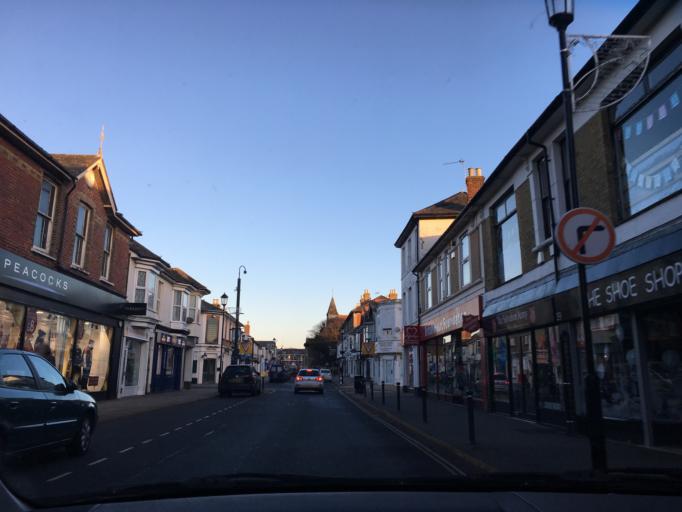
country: GB
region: England
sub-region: Isle of Wight
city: Shanklin
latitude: 50.6308
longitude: -1.1783
